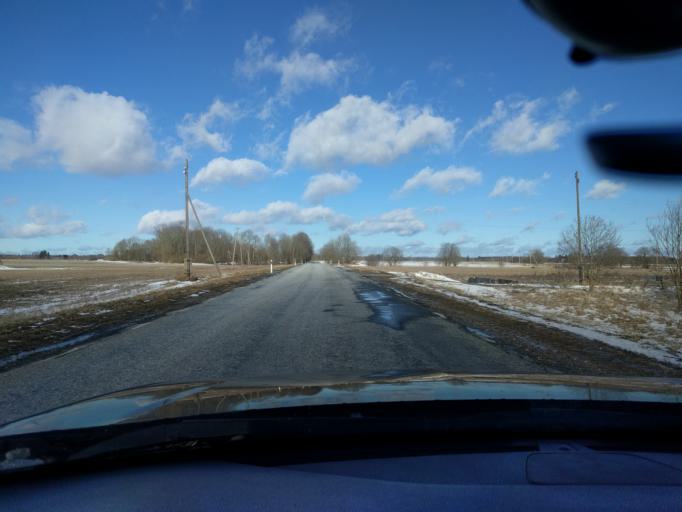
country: EE
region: Harju
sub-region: Raasiku vald
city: Raasiku
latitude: 59.3440
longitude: 25.1507
